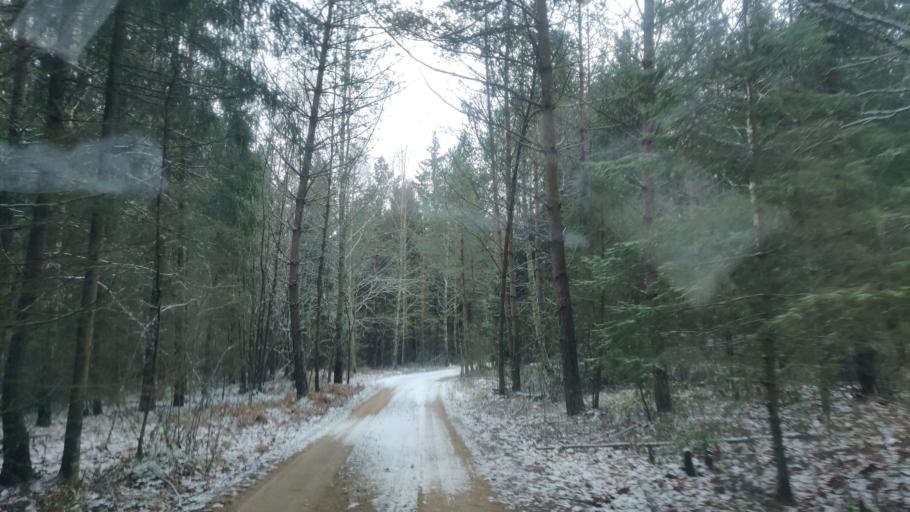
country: LT
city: Trakai
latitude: 54.5717
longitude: 24.9391
